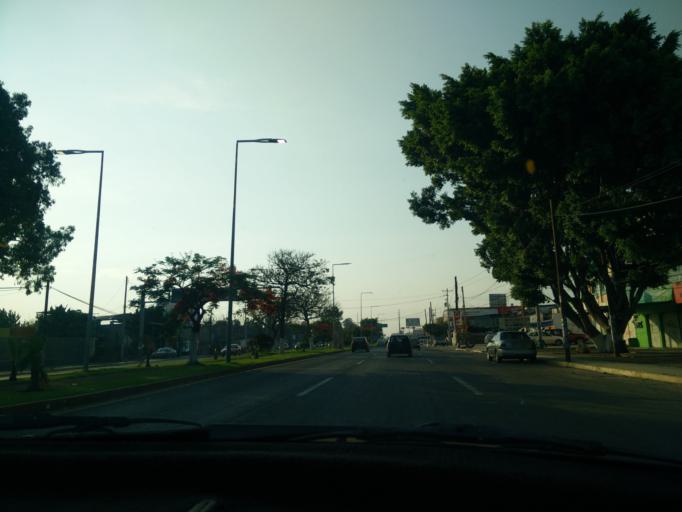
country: MX
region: Oaxaca
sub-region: Santa Maria Atzompa
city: San Jeronimo Yahuiche
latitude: 17.1208
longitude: -96.7628
